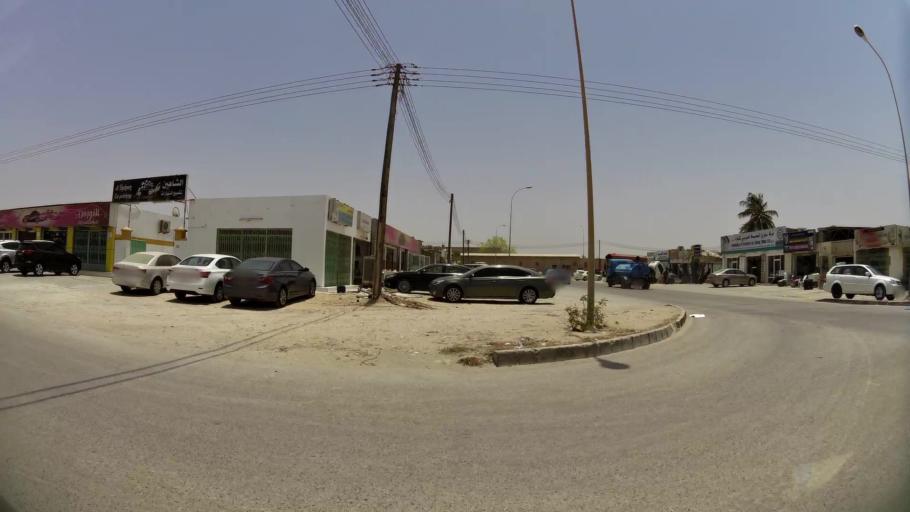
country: OM
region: Zufar
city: Salalah
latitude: 17.0220
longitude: 54.1164
